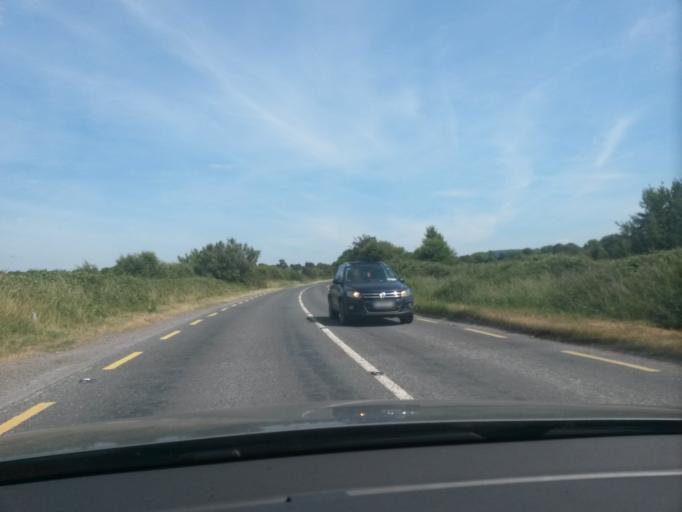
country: IE
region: Leinster
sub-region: Kildare
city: Johnstown
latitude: 53.2059
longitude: -6.6304
